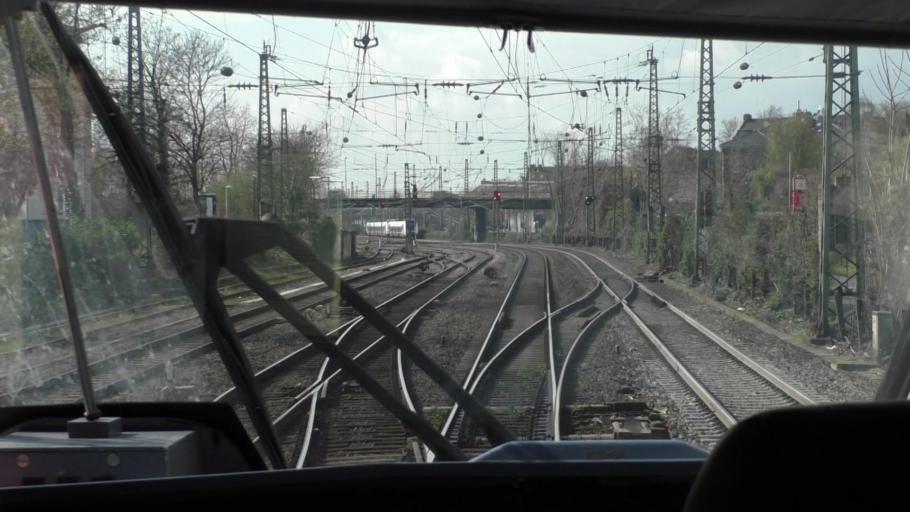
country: DE
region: North Rhine-Westphalia
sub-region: Regierungsbezirk Koln
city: Bonn
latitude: 50.7338
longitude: 7.0914
